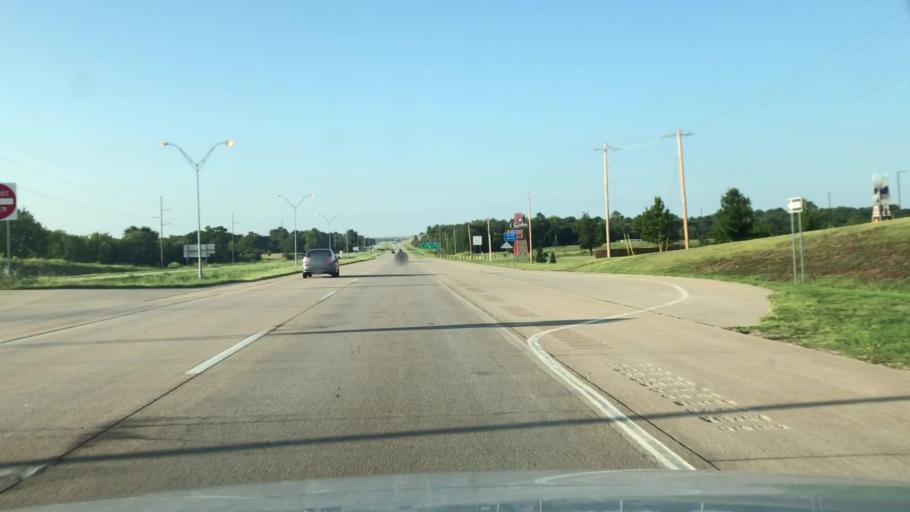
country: US
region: Oklahoma
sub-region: Washington County
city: Bartlesville
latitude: 36.5634
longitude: -95.9295
